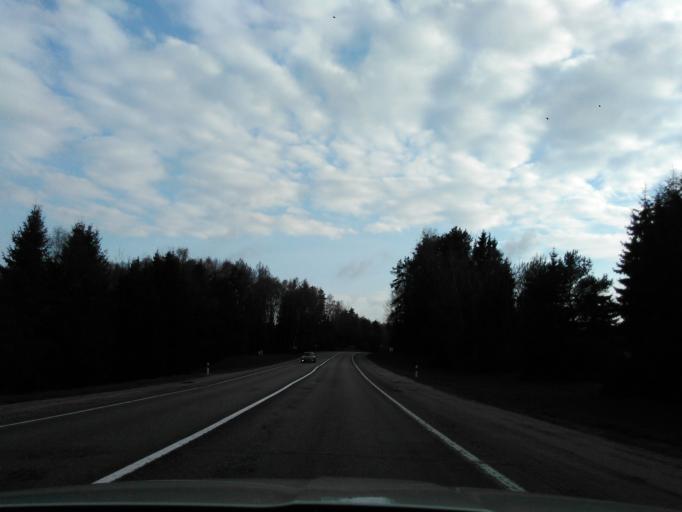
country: BY
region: Minsk
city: Lahoysk
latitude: 54.2889
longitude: 27.8710
